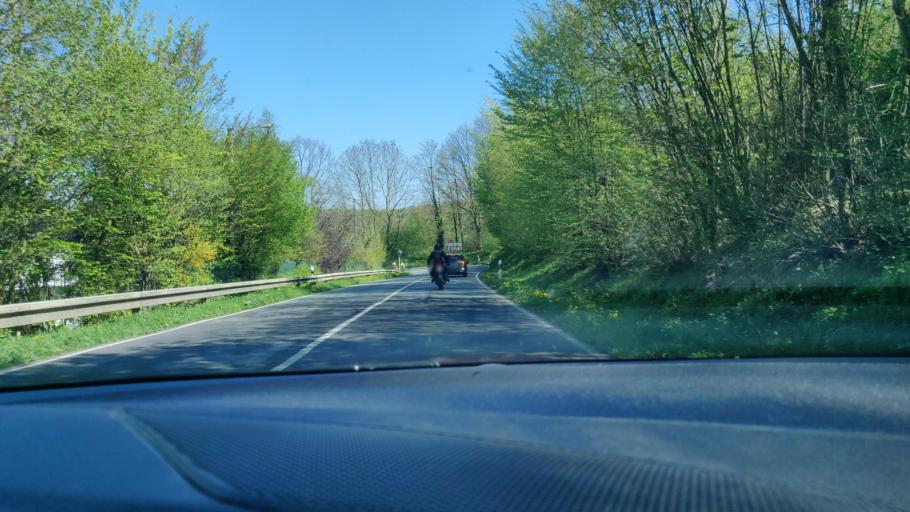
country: DE
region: North Rhine-Westphalia
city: Wulfrath
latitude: 51.2636
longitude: 7.0737
